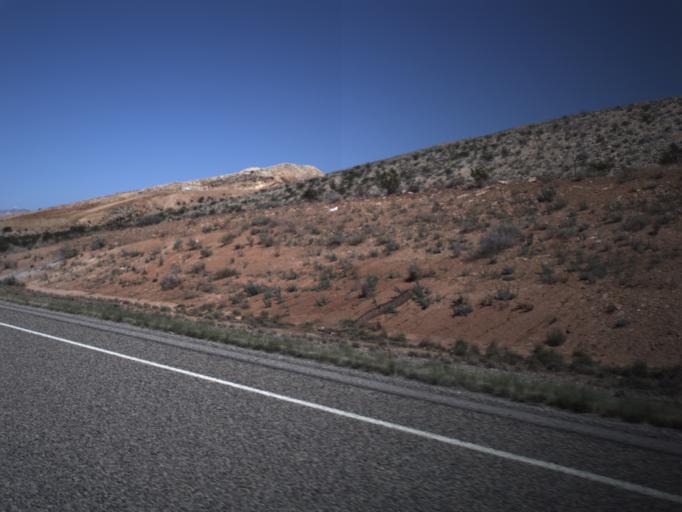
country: US
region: Utah
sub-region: Washington County
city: Saint George
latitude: 37.0213
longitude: -113.5993
